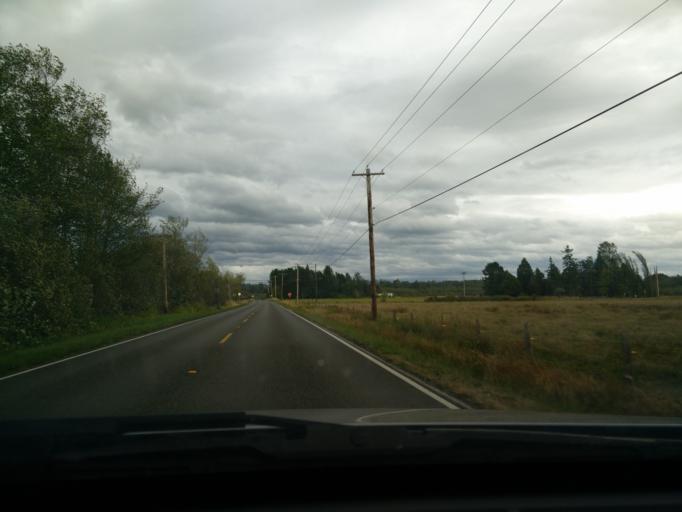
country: US
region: Washington
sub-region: Snohomish County
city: Stanwood
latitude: 48.2685
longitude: -122.3266
